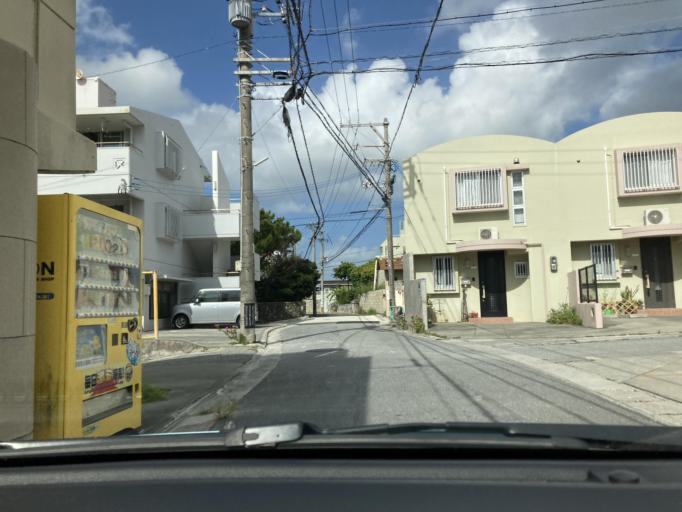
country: JP
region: Okinawa
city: Naha-shi
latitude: 26.2037
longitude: 127.7095
